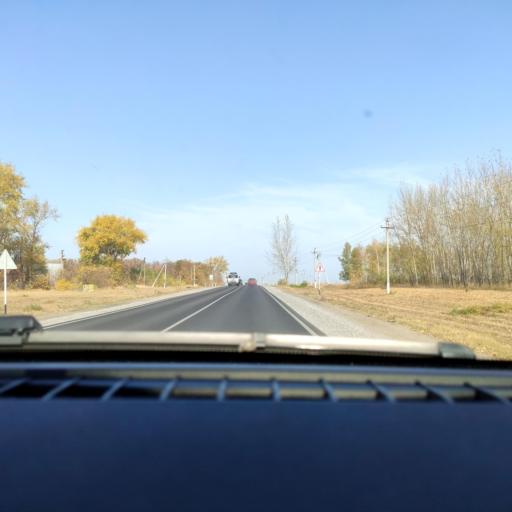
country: RU
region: Voronezj
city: Novaya Usman'
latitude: 51.6834
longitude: 39.3967
